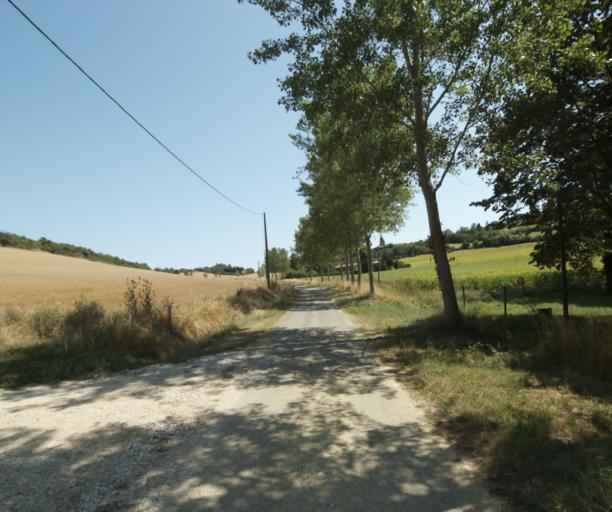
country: FR
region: Midi-Pyrenees
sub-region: Departement de la Haute-Garonne
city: Saint-Felix-Lauragais
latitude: 43.4555
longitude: 1.8808
